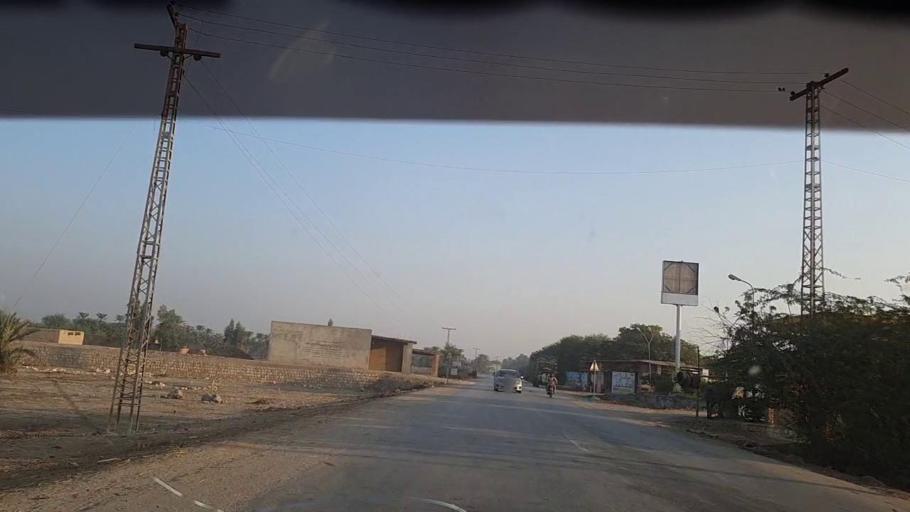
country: PK
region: Sindh
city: Ranipur
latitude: 27.2641
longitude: 68.5232
